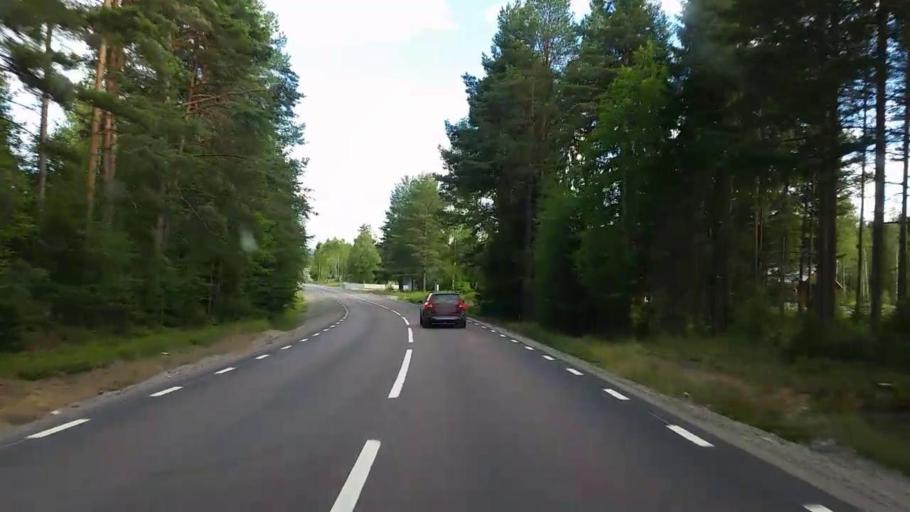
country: SE
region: Gaevleborg
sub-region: Ljusdals Kommun
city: Ljusdal
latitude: 61.8617
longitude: 15.9839
